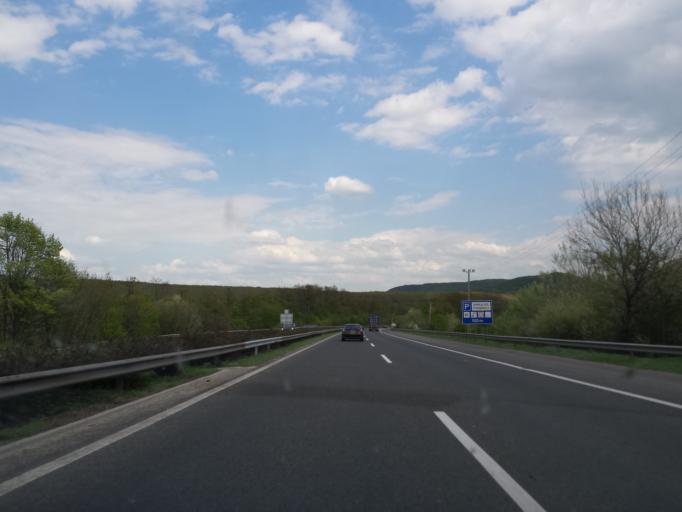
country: HU
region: Komarom-Esztergom
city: Tatabanya
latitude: 47.5754
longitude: 18.4516
